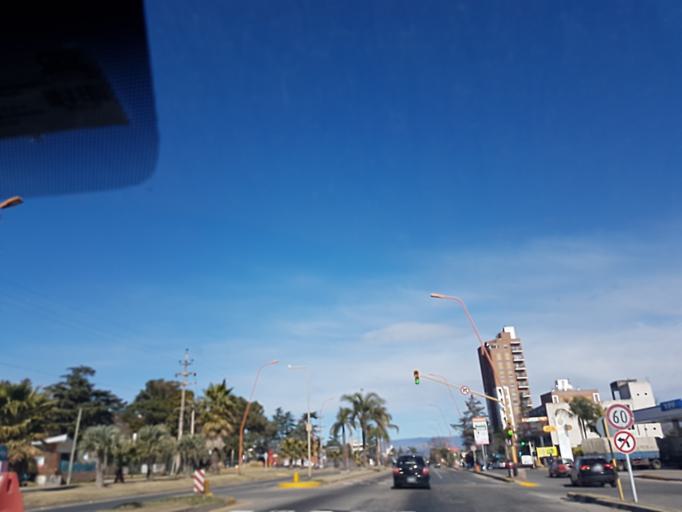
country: AR
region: Cordoba
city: Villa Carlos Paz
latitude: -31.4023
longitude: -64.4701
